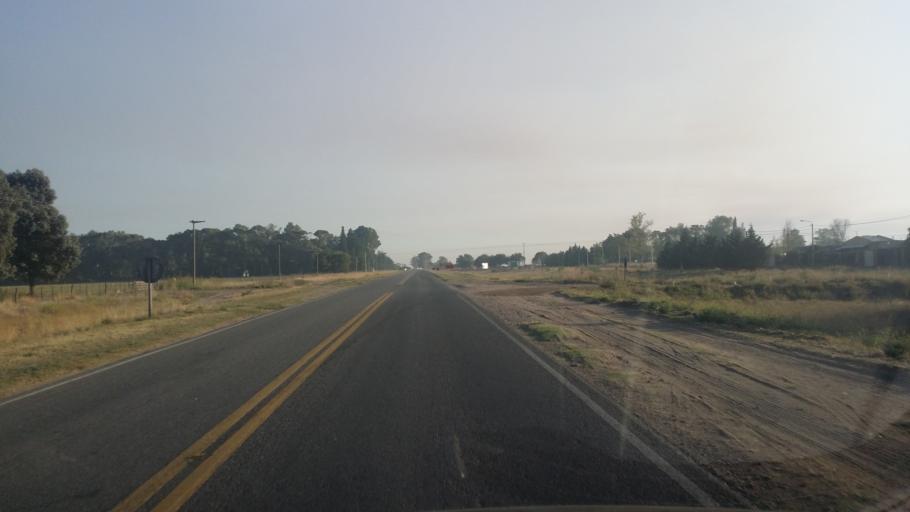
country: AR
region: La Pampa
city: Santa Rosa
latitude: -36.5756
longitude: -64.2811
